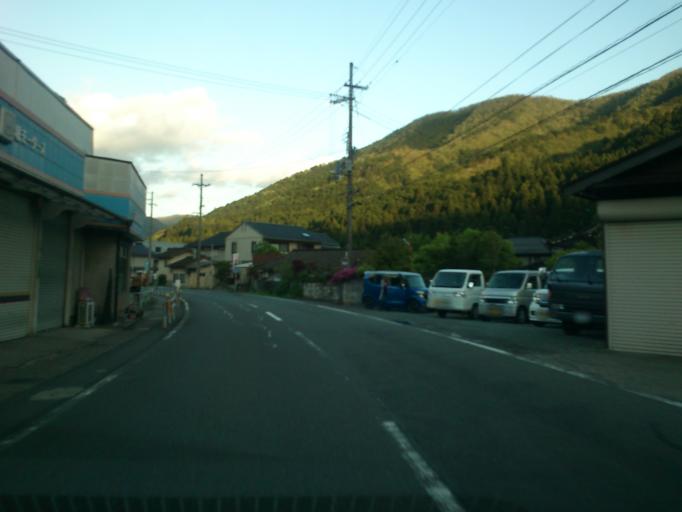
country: JP
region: Kyoto
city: Ayabe
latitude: 35.2598
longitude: 135.3978
